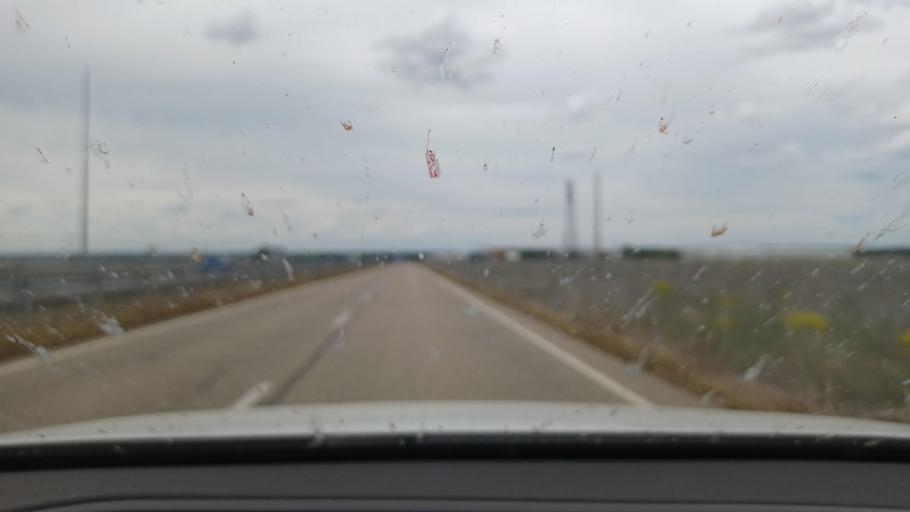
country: ES
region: Castille and Leon
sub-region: Provincia de Valladolid
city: Aldeamayor de San Martin
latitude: 41.4952
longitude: -4.6175
